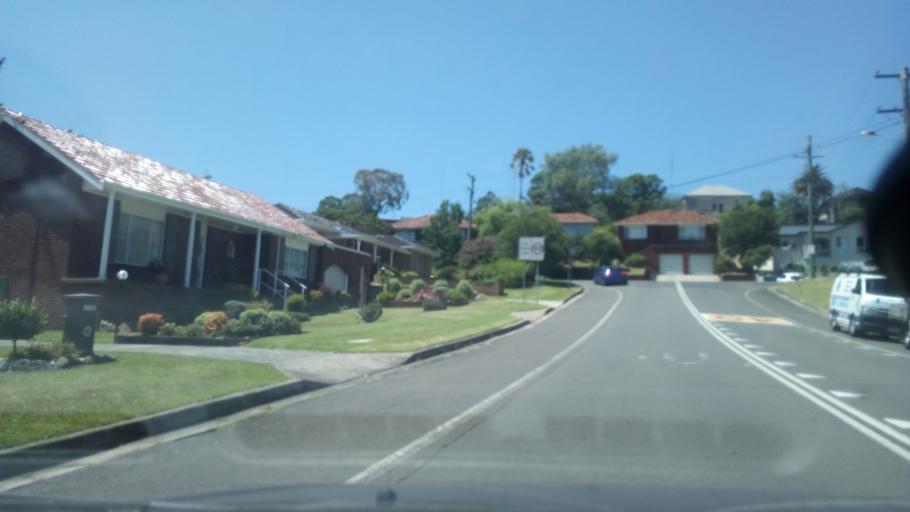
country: AU
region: New South Wales
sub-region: Wollongong
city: West Wollongong
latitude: -34.4268
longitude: 150.8619
